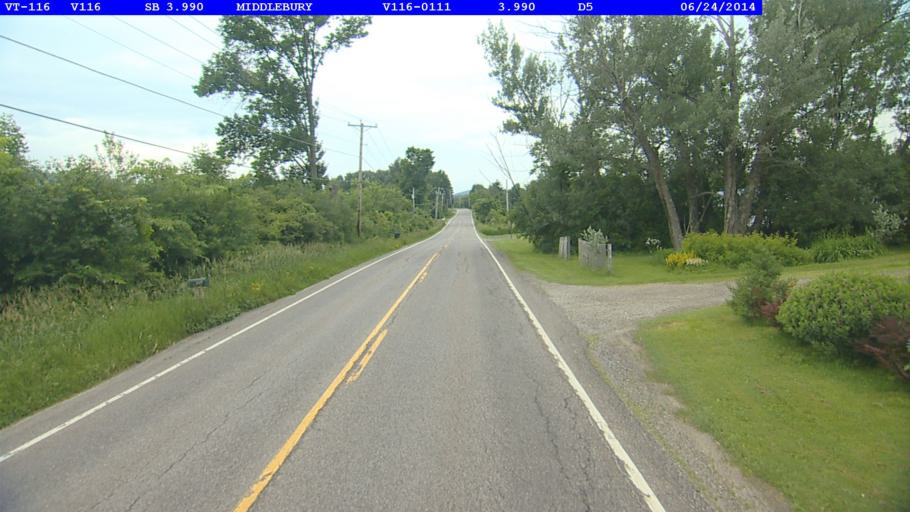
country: US
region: Vermont
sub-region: Addison County
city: Middlebury (village)
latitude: 44.0198
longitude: -73.1025
